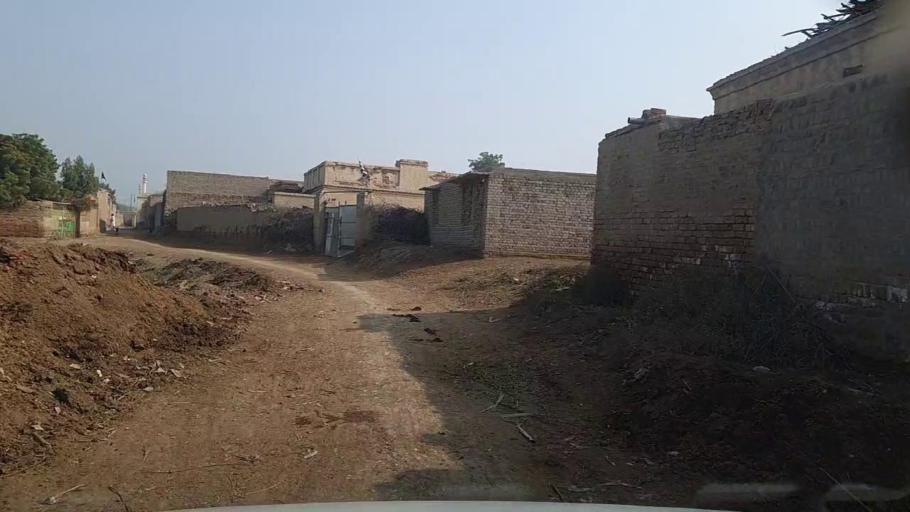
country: PK
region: Sindh
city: Setharja Old
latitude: 27.1401
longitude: 68.5001
